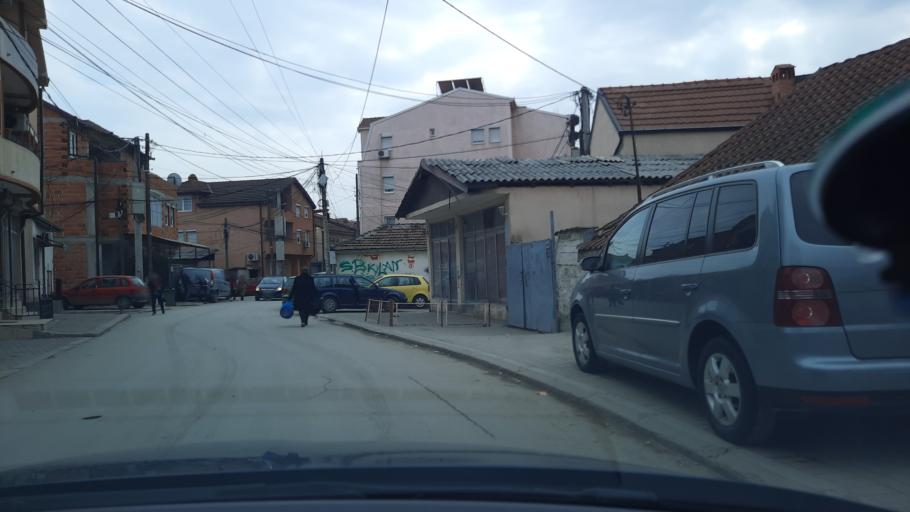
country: MK
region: Cair
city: Cair
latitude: 42.0100
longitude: 21.4407
